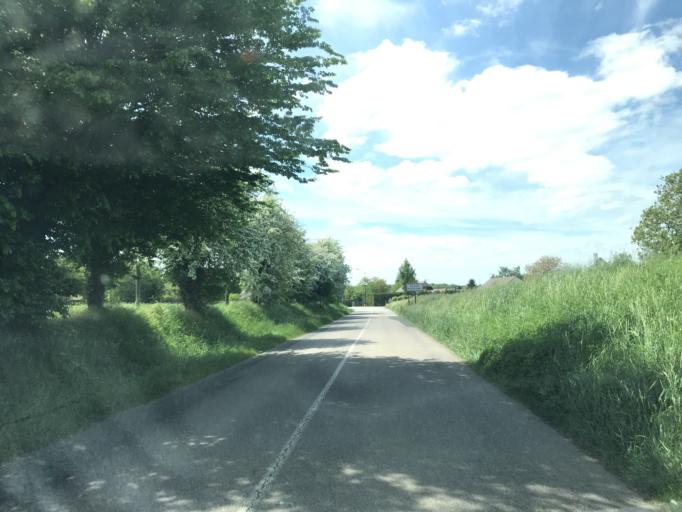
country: FR
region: Haute-Normandie
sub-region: Departement de l'Eure
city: Le Neubourg
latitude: 49.1476
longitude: 0.8375
